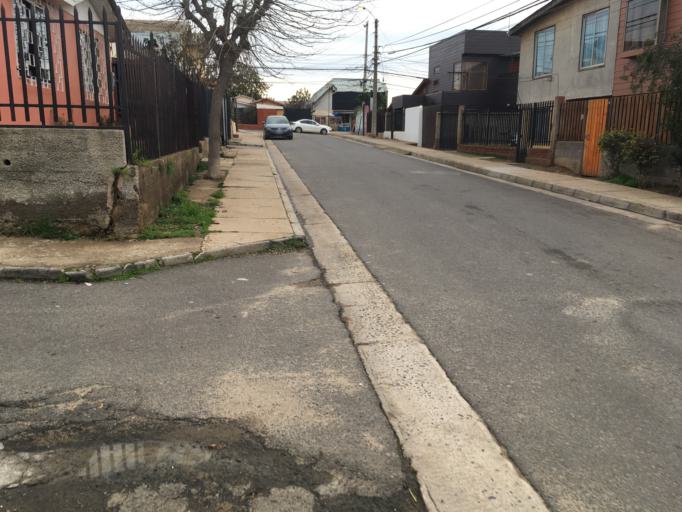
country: CL
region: Valparaiso
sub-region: Provincia de Valparaiso
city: Vina del Mar
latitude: -33.0049
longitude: -71.4965
